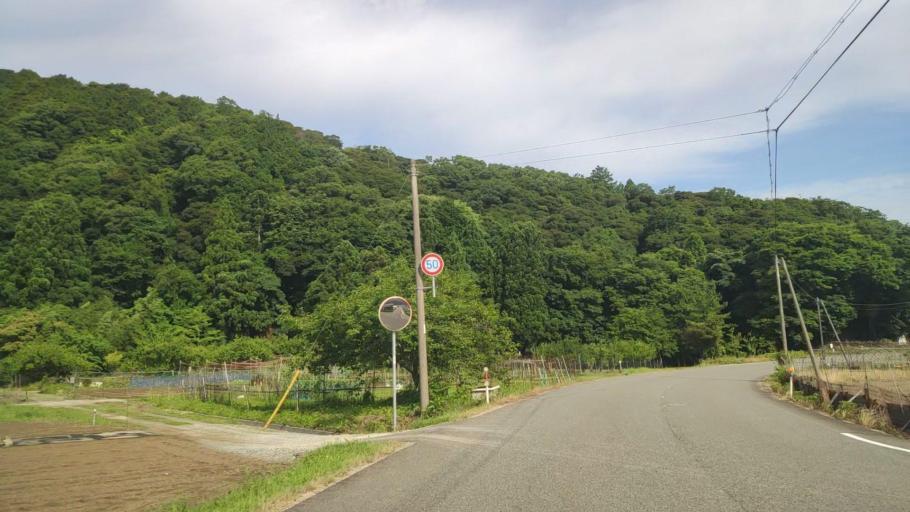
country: JP
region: Hyogo
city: Toyooka
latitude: 35.6344
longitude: 134.8373
